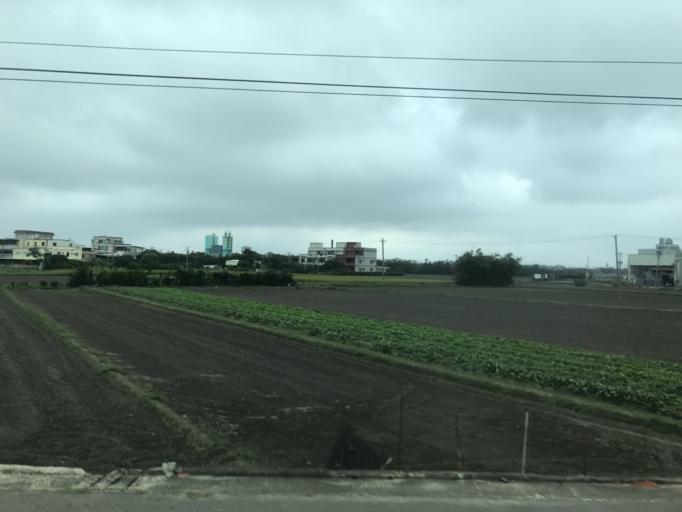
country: TW
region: Taiwan
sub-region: Hsinchu
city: Hsinchu
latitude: 24.8275
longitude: 120.9553
